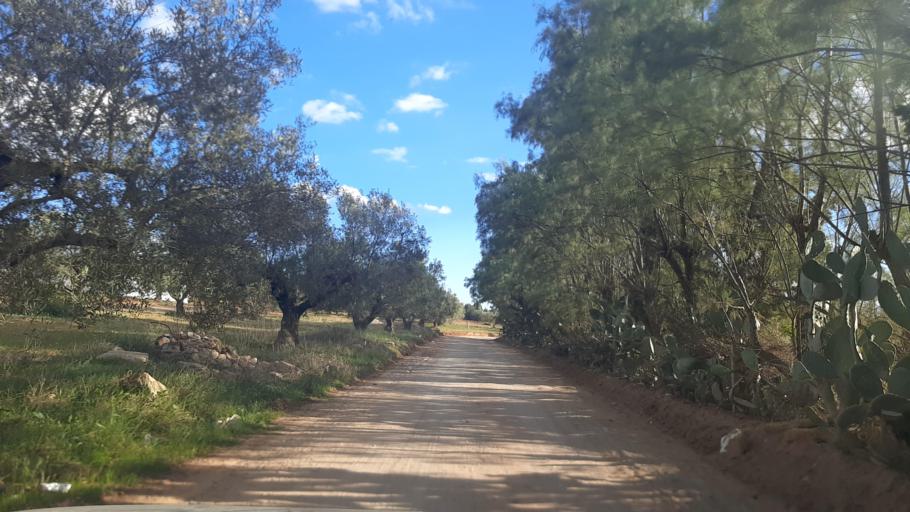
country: TN
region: Nabul
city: Al Hammamat
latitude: 36.4265
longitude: 10.5073
